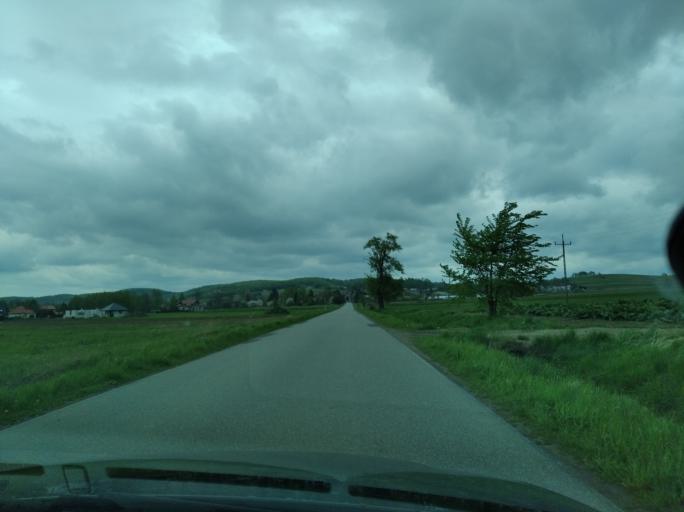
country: PL
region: Subcarpathian Voivodeship
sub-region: Powiat sanocki
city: Dlugie
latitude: 49.5981
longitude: 22.0508
